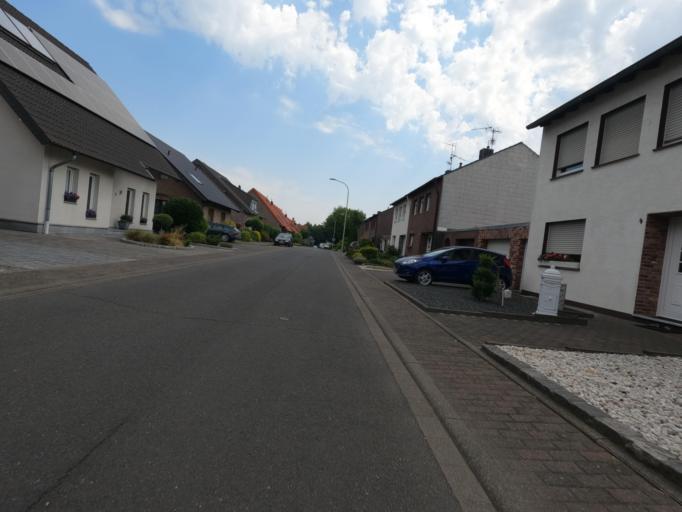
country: DE
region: North Rhine-Westphalia
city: Baesweiler
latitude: 50.9167
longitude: 6.1915
